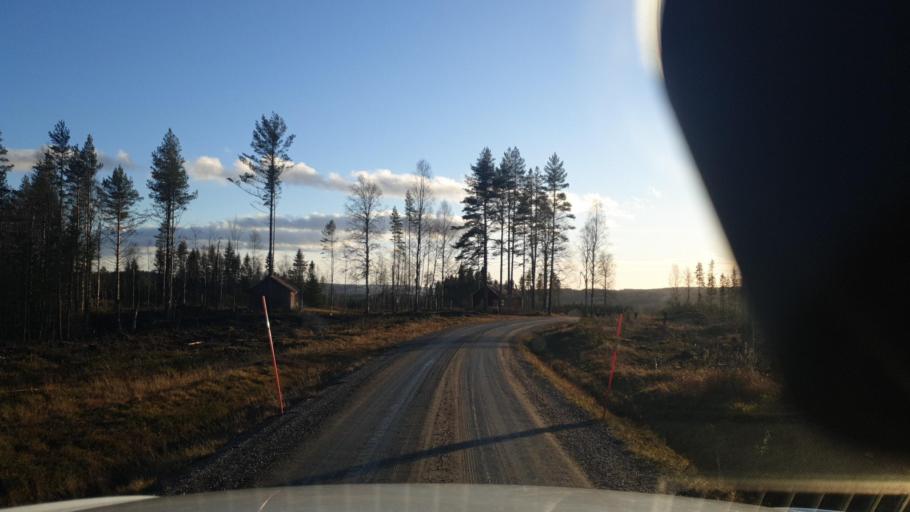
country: SE
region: Vaermland
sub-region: Eda Kommun
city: Charlottenberg
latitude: 60.0570
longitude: 12.5267
